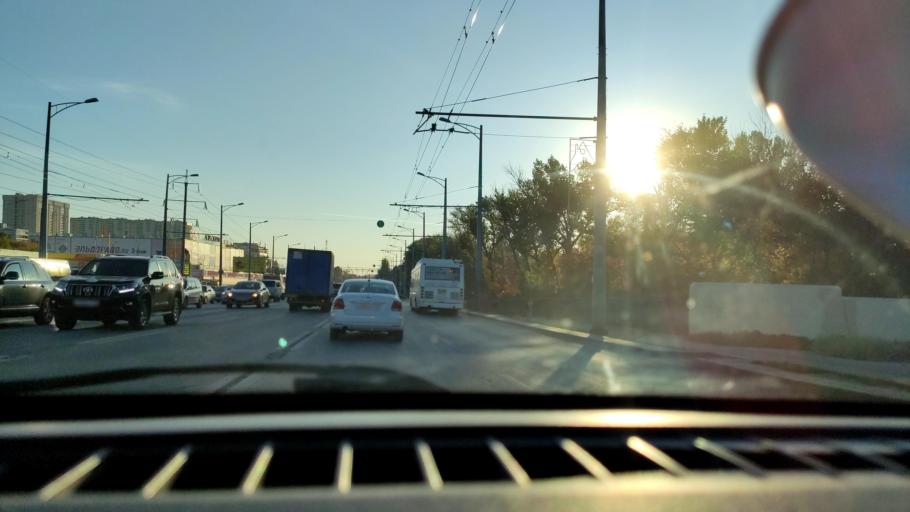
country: RU
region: Samara
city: Samara
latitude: 53.2151
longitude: 50.1836
